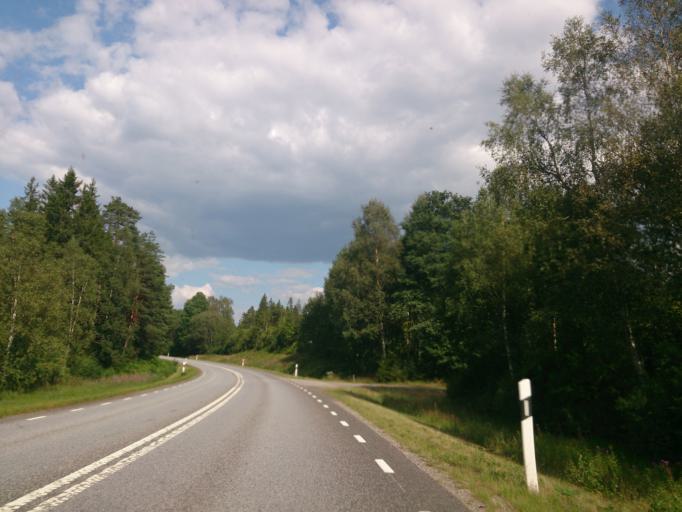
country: SE
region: Joenkoeping
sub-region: Gislaveds Kommun
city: Smalandsstenar
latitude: 57.1562
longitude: 13.4898
